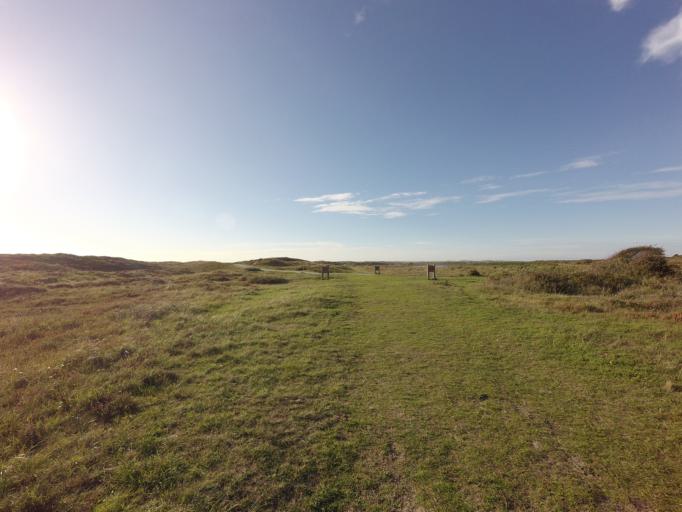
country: NL
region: North Holland
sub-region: Gemeente Den Helder
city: Den Helder
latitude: 53.0193
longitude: 4.7229
